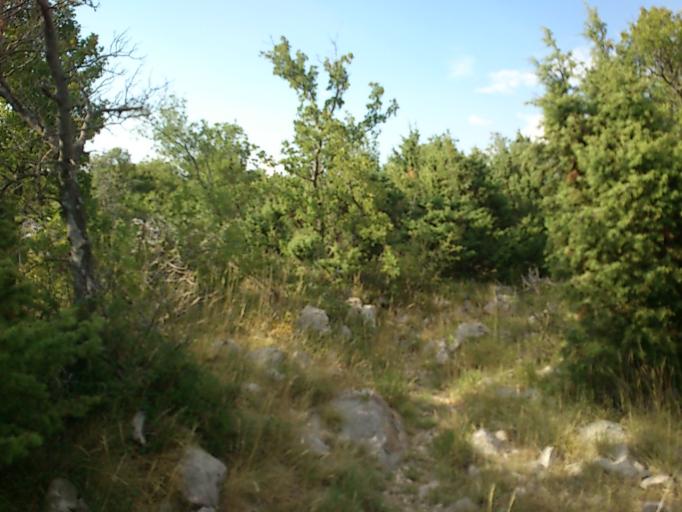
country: HR
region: Primorsko-Goranska
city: Banjol
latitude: 44.7547
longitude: 14.8987
